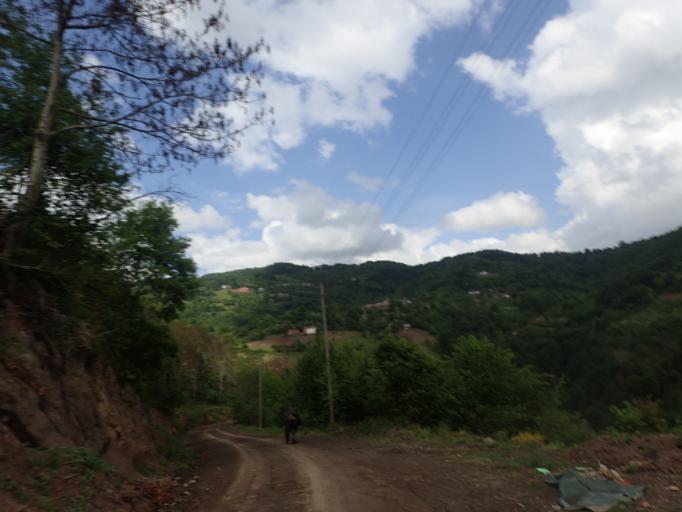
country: TR
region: Ordu
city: Akkus
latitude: 40.9050
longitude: 36.8967
